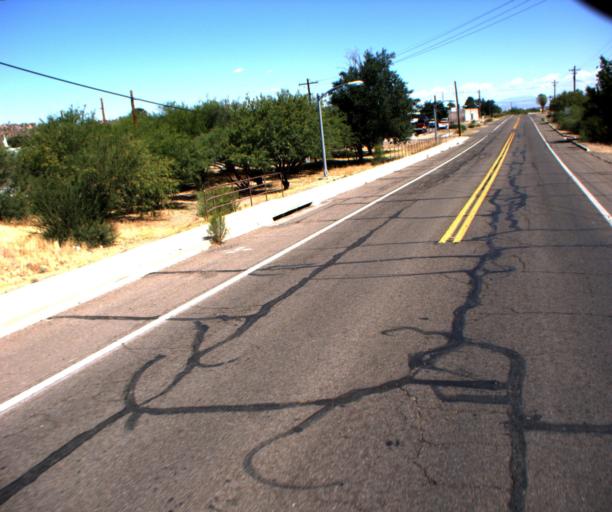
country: US
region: Arizona
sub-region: Pinal County
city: Mammoth
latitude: 32.7318
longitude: -110.6476
